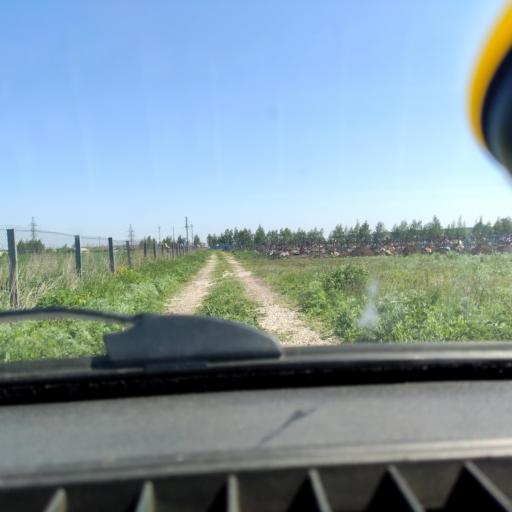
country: RU
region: Samara
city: Povolzhskiy
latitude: 53.6310
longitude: 49.6556
